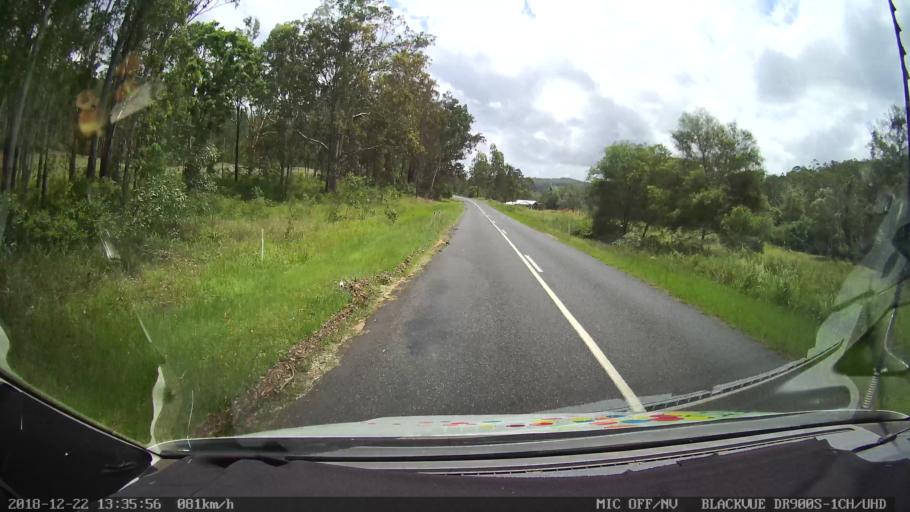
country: AU
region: New South Wales
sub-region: Clarence Valley
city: Coutts Crossing
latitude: -29.8764
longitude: 152.8003
